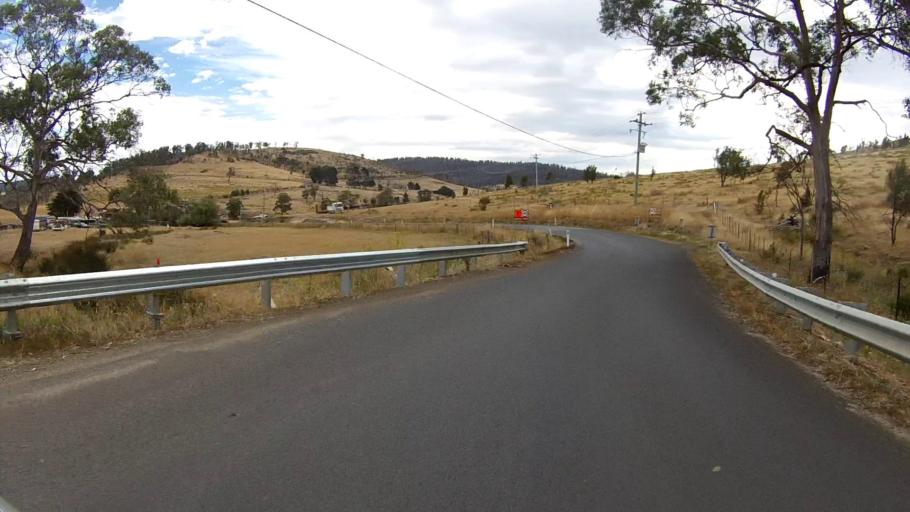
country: AU
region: Tasmania
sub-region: Sorell
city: Sorell
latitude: -42.8737
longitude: 147.7027
